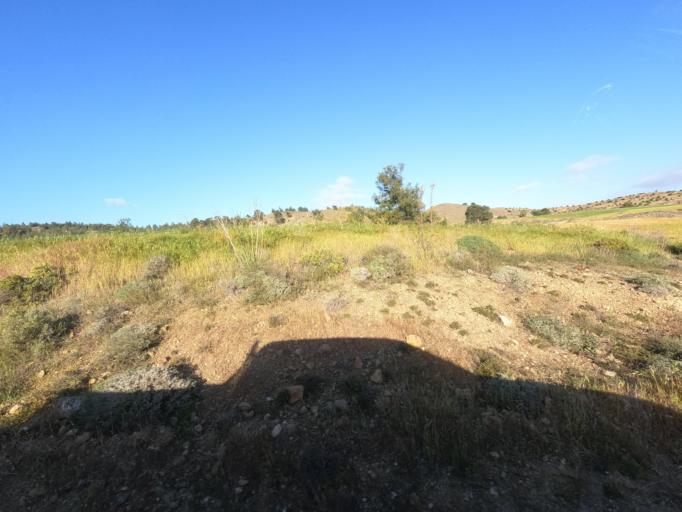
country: CY
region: Lefkosia
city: Peristerona
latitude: 35.0676
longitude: 33.0442
